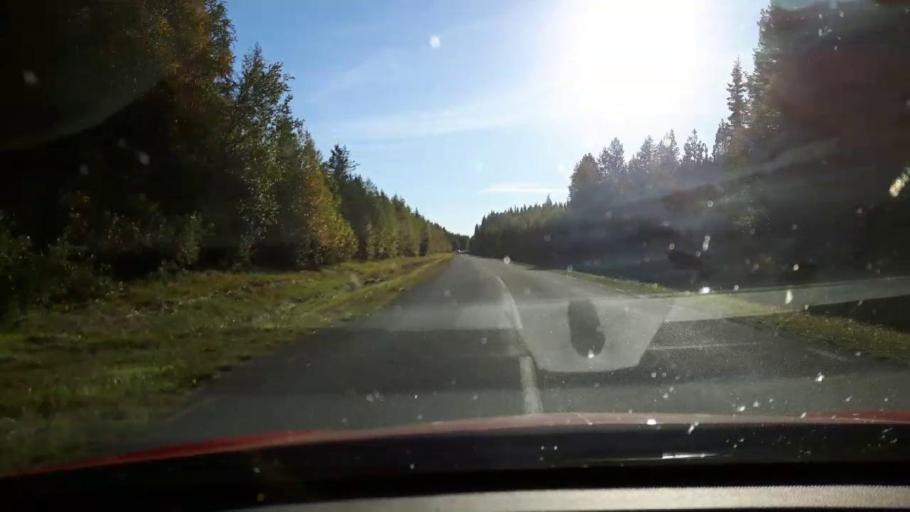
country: SE
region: Jaemtland
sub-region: OEstersunds Kommun
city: Lit
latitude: 63.8263
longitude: 14.8615
